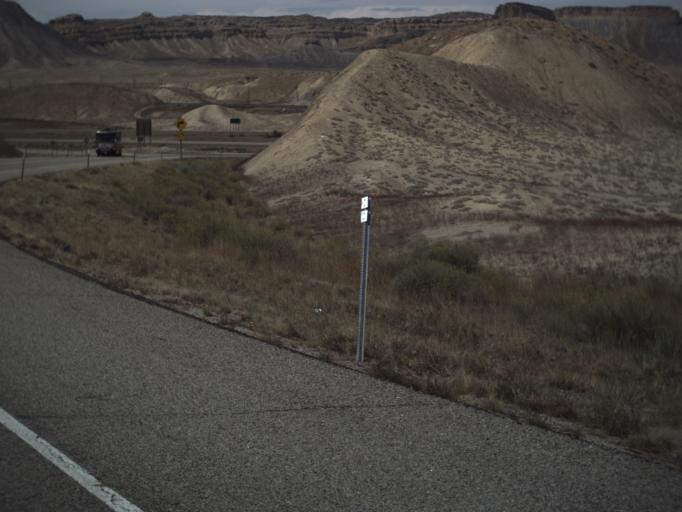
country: US
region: Utah
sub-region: Grand County
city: Moab
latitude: 38.9364
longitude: -109.8307
